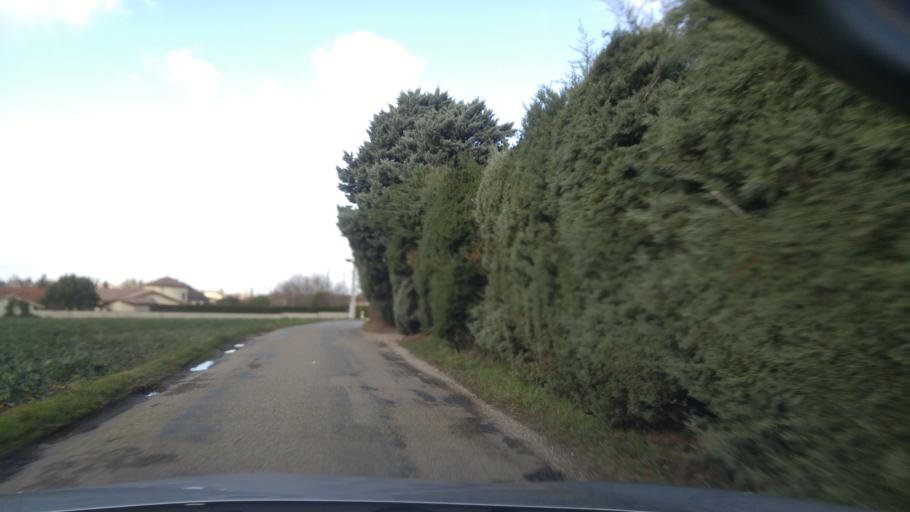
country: FR
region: Rhone-Alpes
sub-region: Departement de l'Isere
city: Roche
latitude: 45.5816
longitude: 5.1708
